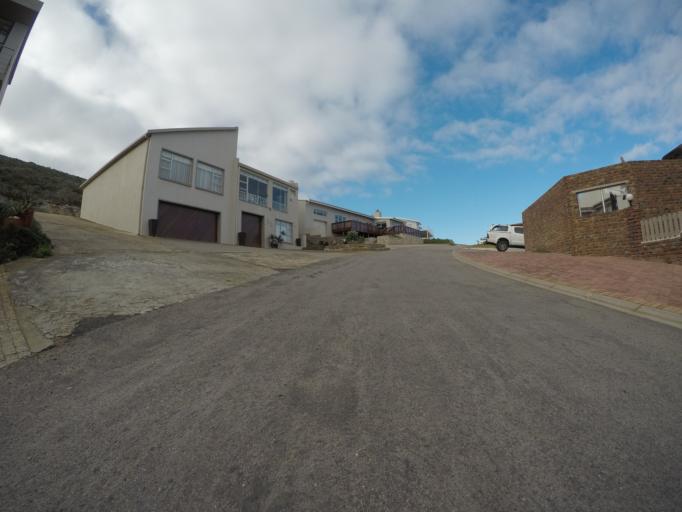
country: ZA
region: Western Cape
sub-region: Eden District Municipality
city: Riversdale
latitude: -34.4312
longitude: 21.3301
